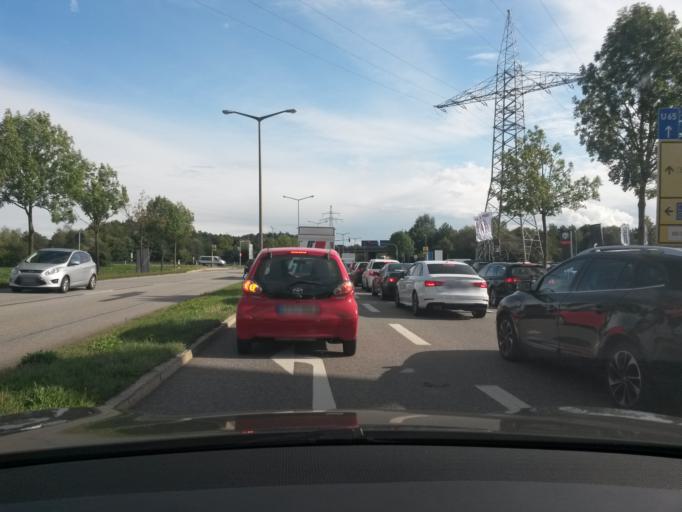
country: DE
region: Bavaria
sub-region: Upper Palatinate
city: Obertraubling
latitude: 49.0002
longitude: 12.1490
